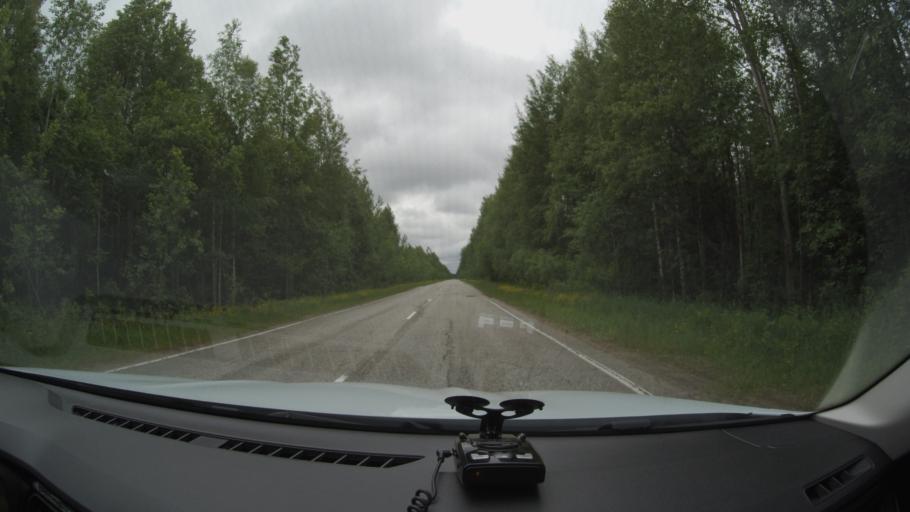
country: RU
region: Komi Republic
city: Nizhniy Odes
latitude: 63.6262
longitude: 54.6230
